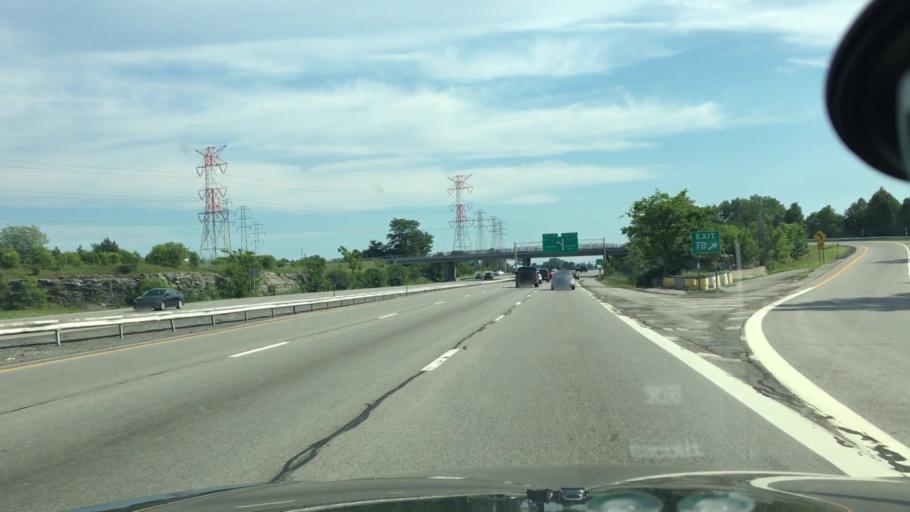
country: US
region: New York
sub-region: Erie County
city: Williamsville
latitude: 42.9588
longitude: -78.7666
